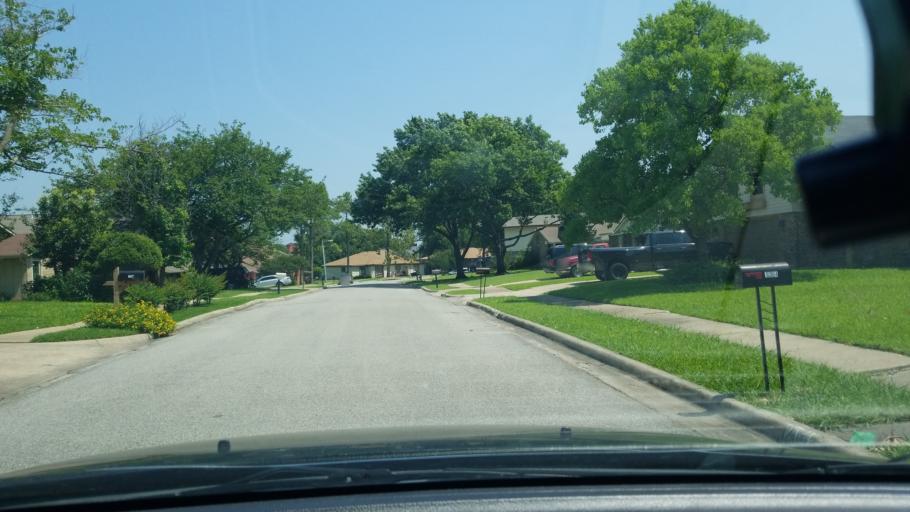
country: US
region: Texas
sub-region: Dallas County
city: Sunnyvale
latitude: 32.8286
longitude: -96.6129
